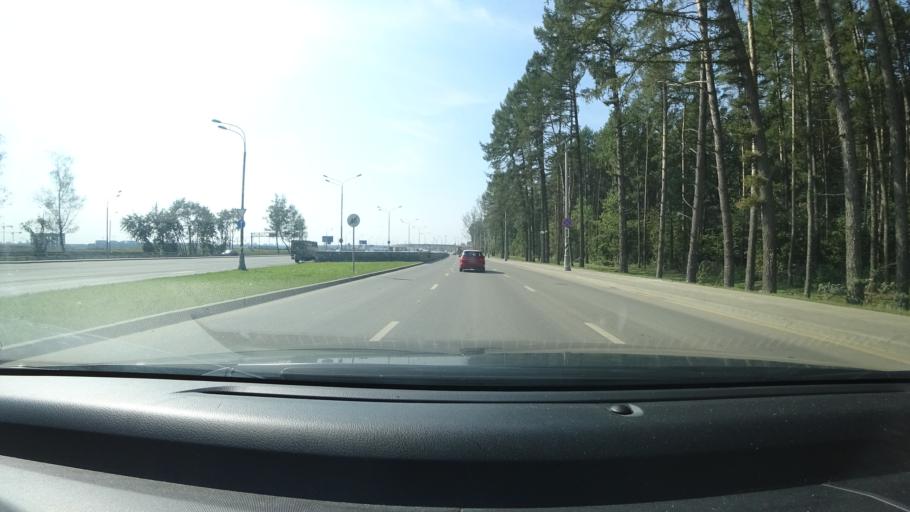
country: RU
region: Moskovskaya
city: Kommunarka
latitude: 55.5767
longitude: 37.4602
